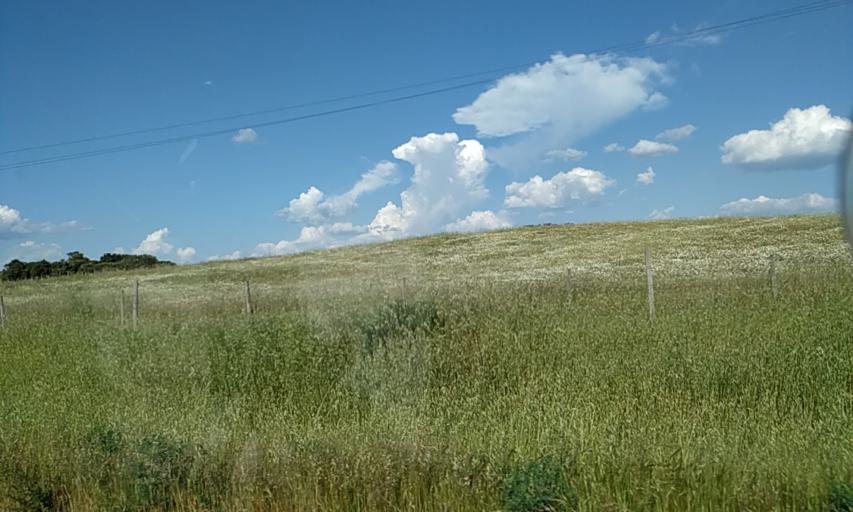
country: PT
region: Portalegre
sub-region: Fronteira
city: Fronteira
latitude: 39.0115
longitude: -7.4676
